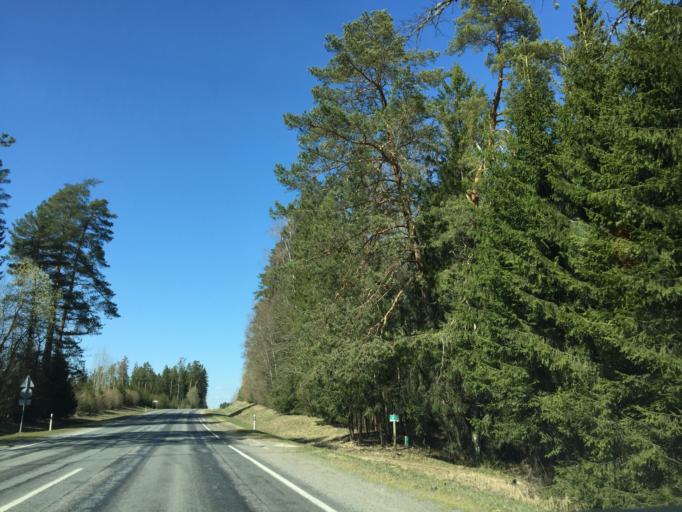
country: EE
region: Viljandimaa
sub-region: Viljandi linn
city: Viljandi
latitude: 58.2867
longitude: 25.5832
